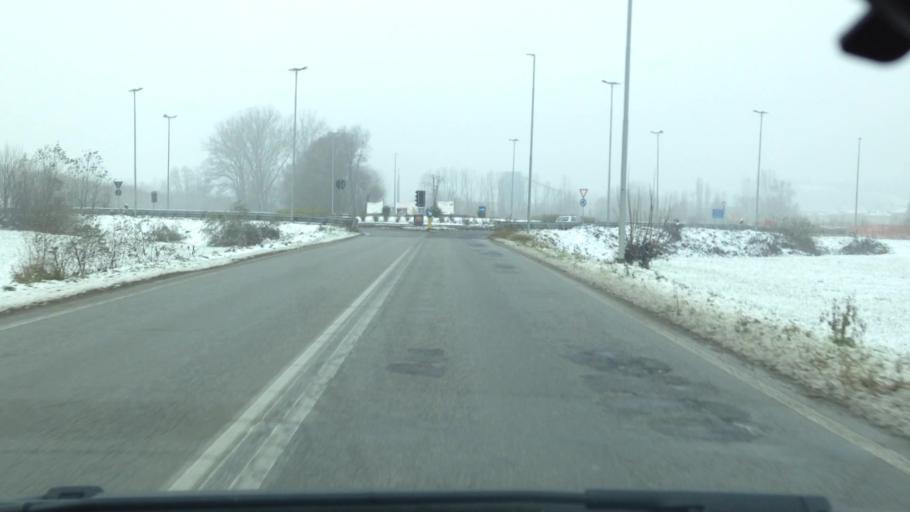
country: IT
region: Piedmont
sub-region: Provincia di Asti
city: Montegrosso
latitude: 44.8221
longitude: 8.2267
